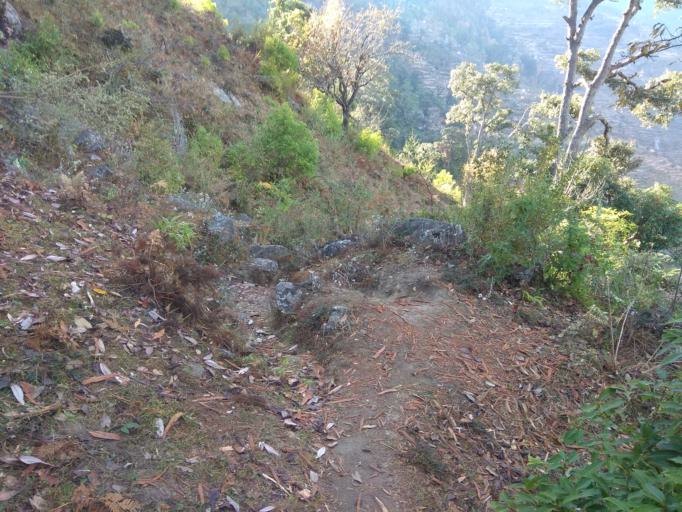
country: NP
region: Mid Western
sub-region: Karnali Zone
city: Jumla
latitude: 29.3139
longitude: 81.7266
